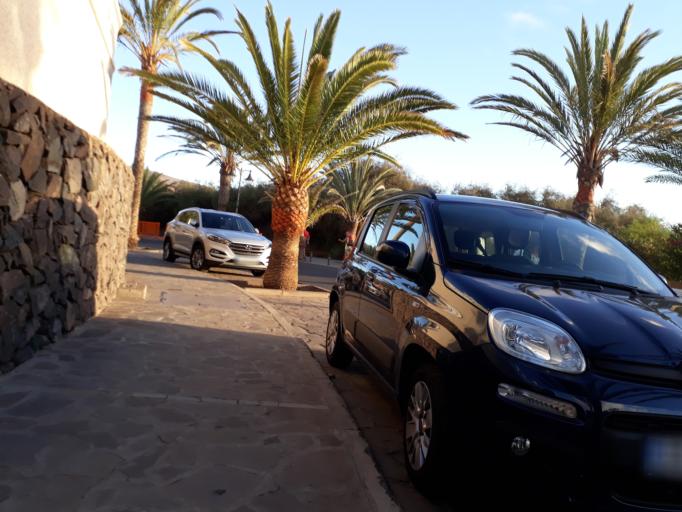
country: ES
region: Canary Islands
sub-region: Provincia de Santa Cruz de Tenerife
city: Alajero
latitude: 28.0865
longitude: -17.3384
